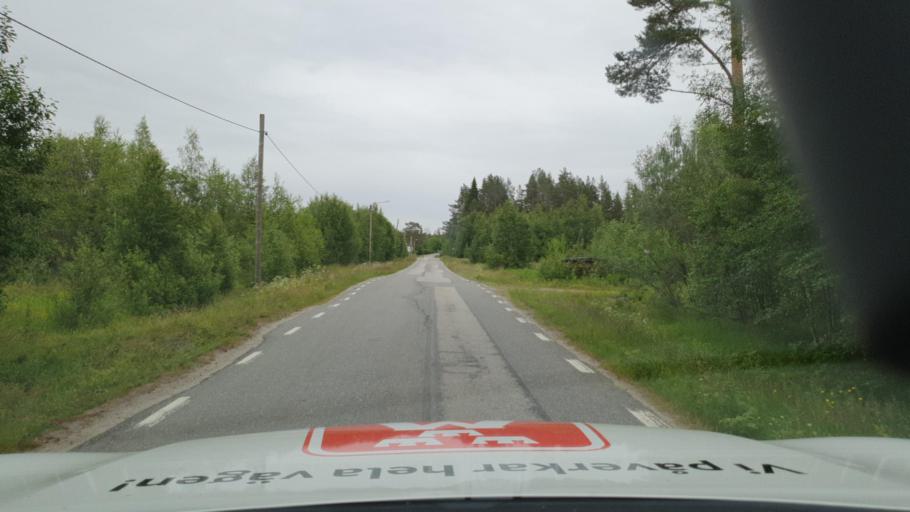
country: SE
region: Vaesterbotten
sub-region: Nordmalings Kommun
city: Nordmaling
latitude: 63.4986
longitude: 19.4243
